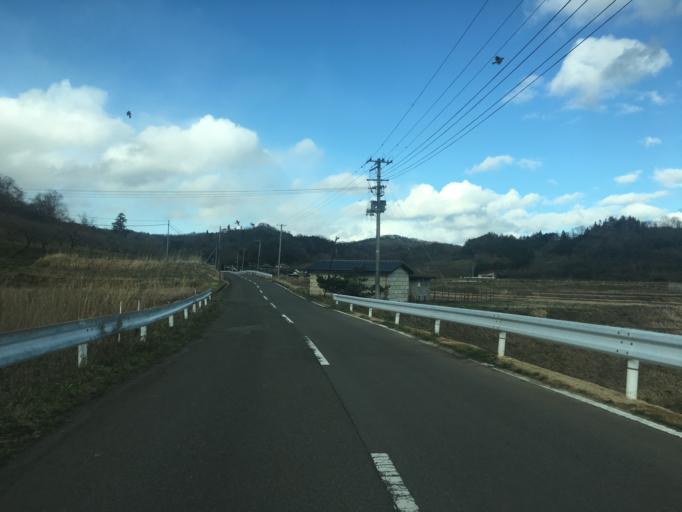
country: JP
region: Fukushima
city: Yanagawamachi-saiwaicho
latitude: 37.8816
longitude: 140.5993
